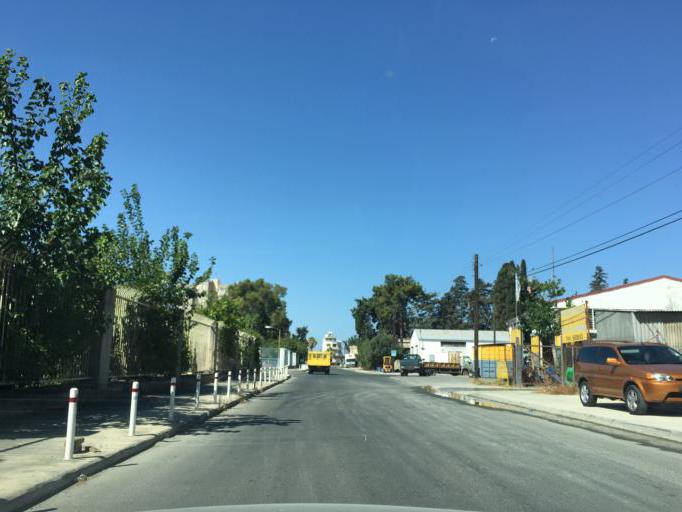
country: CY
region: Limassol
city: Limassol
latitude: 34.6635
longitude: 33.0199
